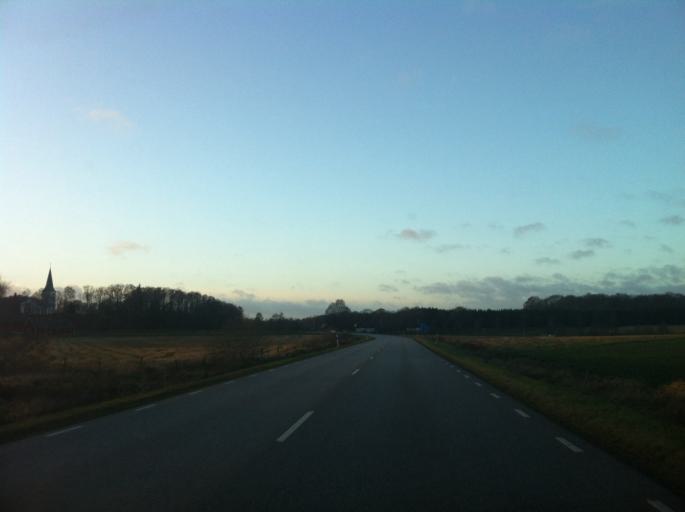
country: SE
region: Skane
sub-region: Hoors Kommun
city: Hoeoer
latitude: 55.9431
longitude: 13.4731
